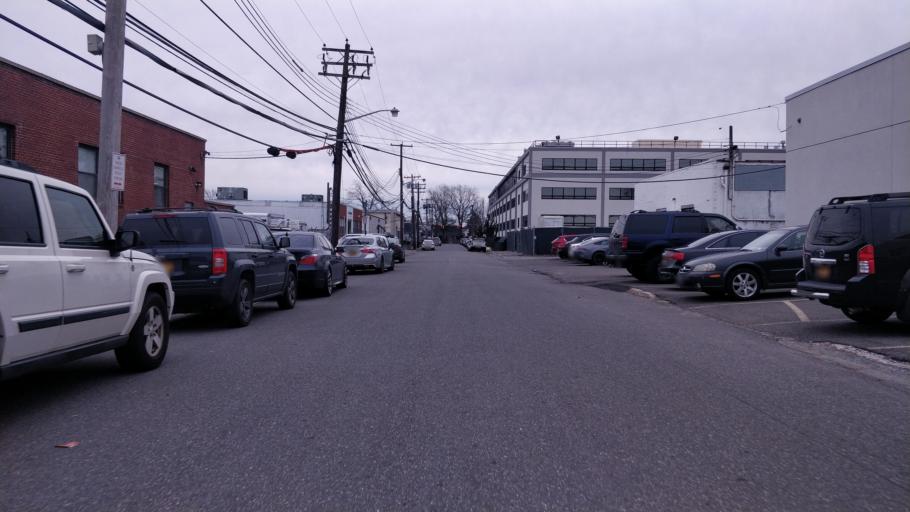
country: US
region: New York
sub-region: Nassau County
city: Salisbury
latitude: 40.7572
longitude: -73.5577
